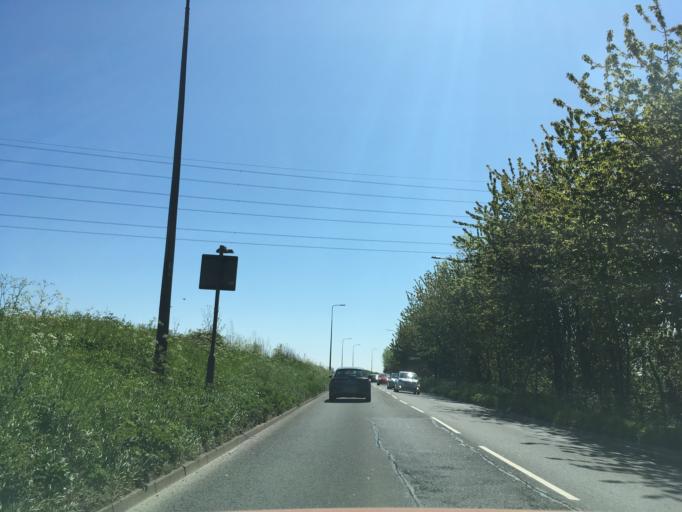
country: GB
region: Wales
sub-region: Cardiff
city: Cardiff
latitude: 51.4891
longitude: -3.1271
